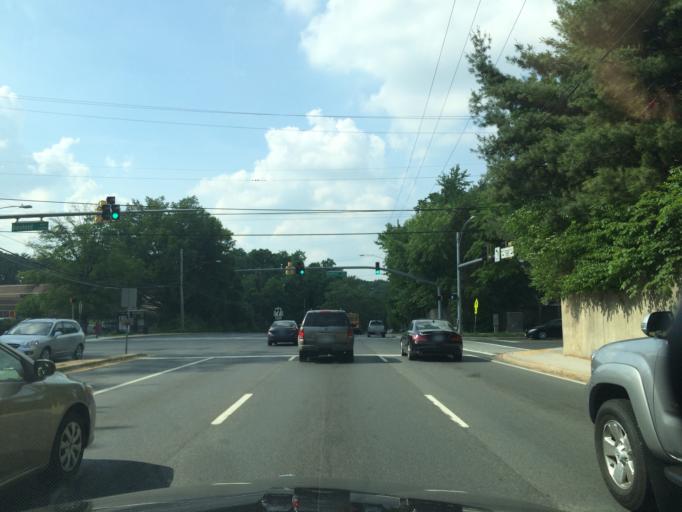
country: US
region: Maryland
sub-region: Montgomery County
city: North Kensington
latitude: 39.0384
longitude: -77.0755
